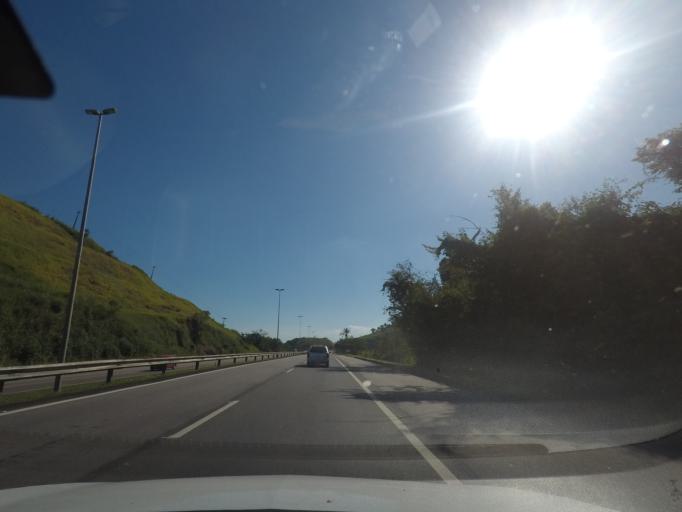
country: BR
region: Rio de Janeiro
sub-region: Guapimirim
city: Guapimirim
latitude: -22.6306
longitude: -43.0513
